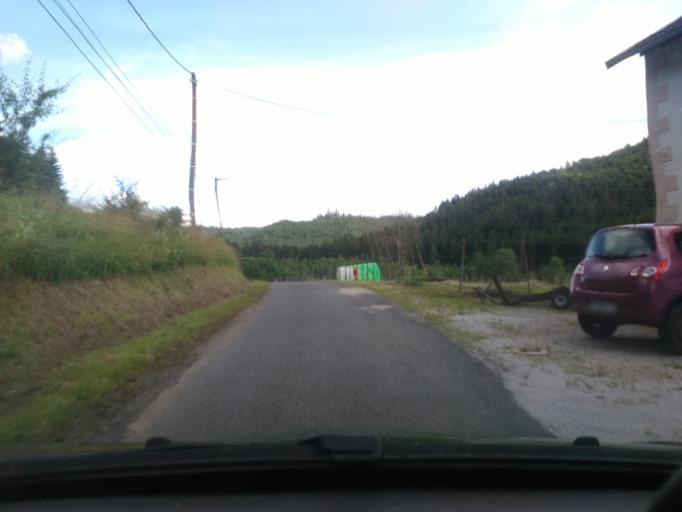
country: FR
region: Lorraine
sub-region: Departement des Vosges
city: Taintrux
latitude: 48.2451
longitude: 6.8086
